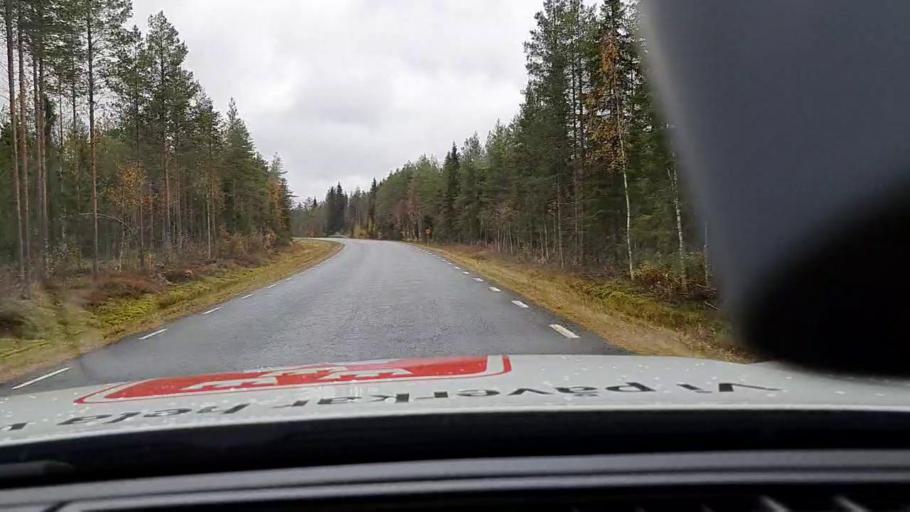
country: SE
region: Norrbotten
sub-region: Haparanda Kommun
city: Haparanda
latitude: 65.9027
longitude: 23.8335
